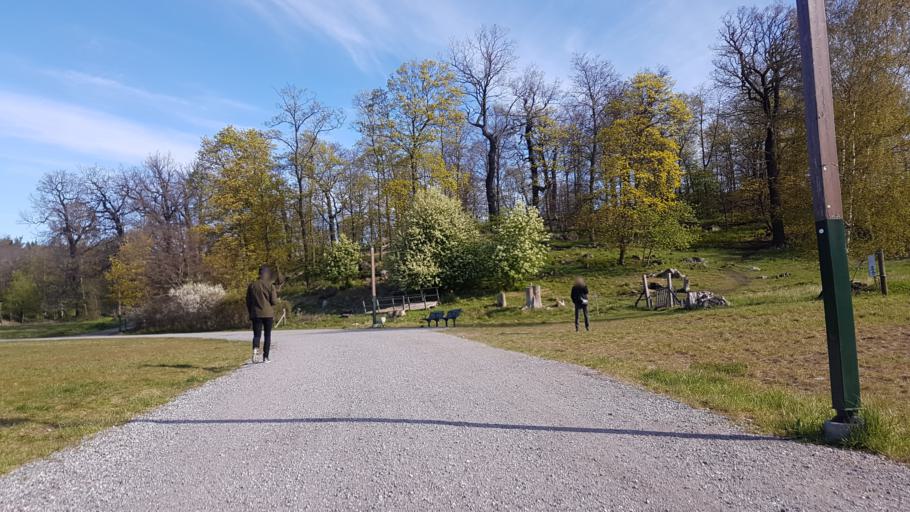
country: SE
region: Stockholm
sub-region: Stockholms Kommun
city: OEstermalm
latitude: 59.3614
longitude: 18.0963
